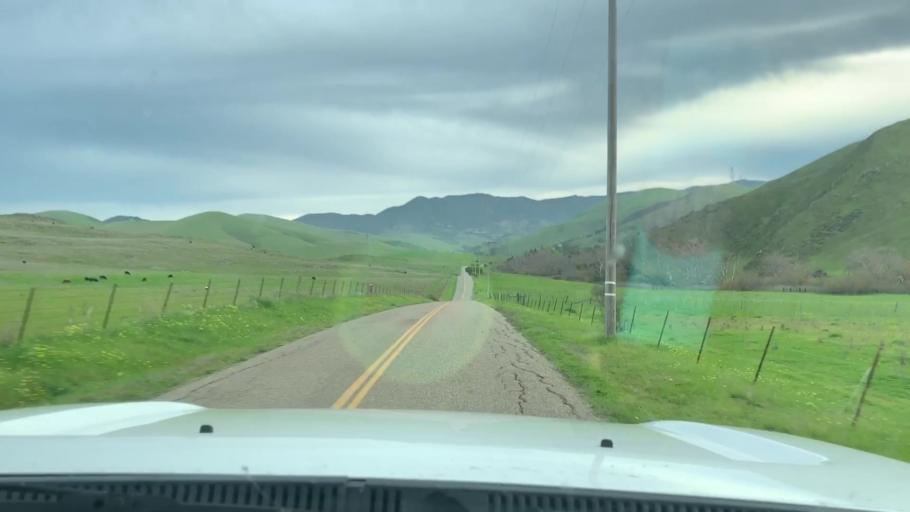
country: US
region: California
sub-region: San Luis Obispo County
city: Morro Bay
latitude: 35.3725
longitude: -120.7995
